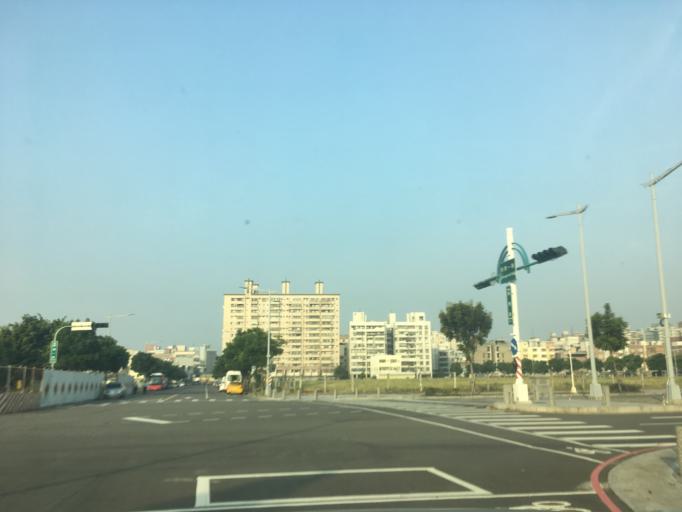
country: TW
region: Taiwan
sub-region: Taichung City
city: Taichung
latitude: 24.1867
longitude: 120.6736
